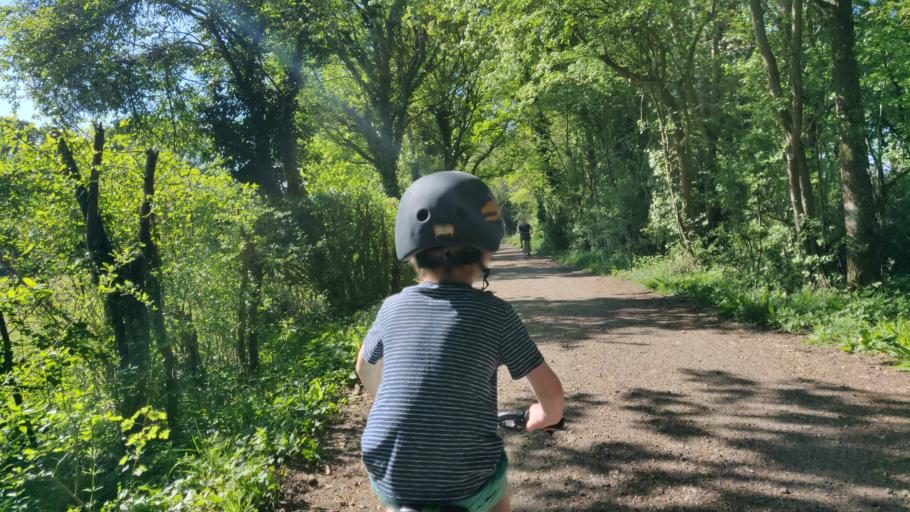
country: GB
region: England
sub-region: West Sussex
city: Southwater
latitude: 51.0603
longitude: -0.3864
